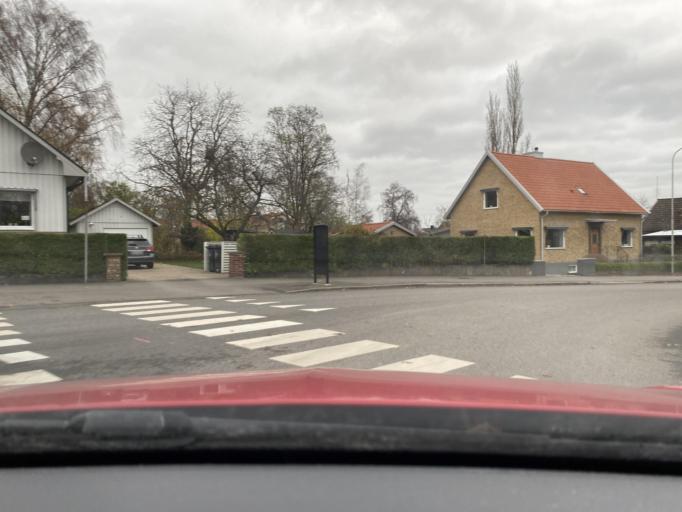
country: SE
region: Skane
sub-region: Hassleholms Kommun
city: Hassleholm
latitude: 56.1614
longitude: 13.7536
